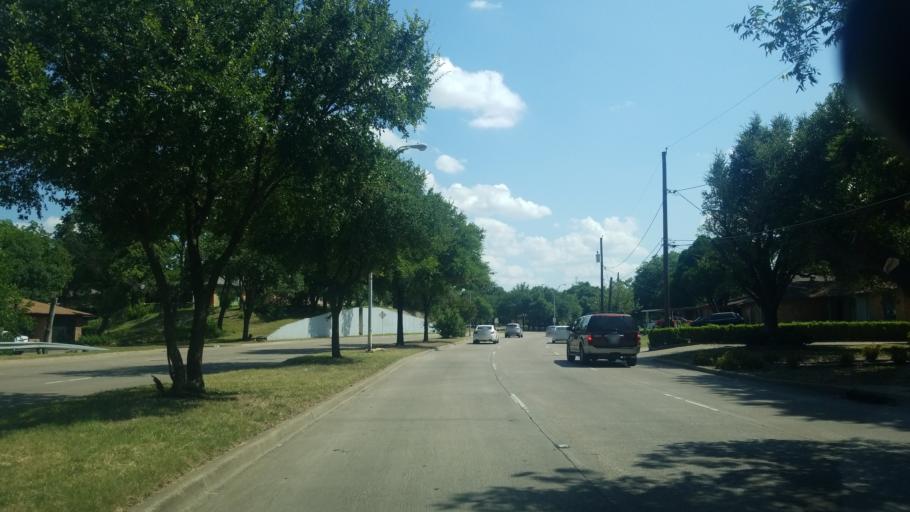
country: US
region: Texas
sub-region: Dallas County
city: Dallas
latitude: 32.7277
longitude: -96.7989
